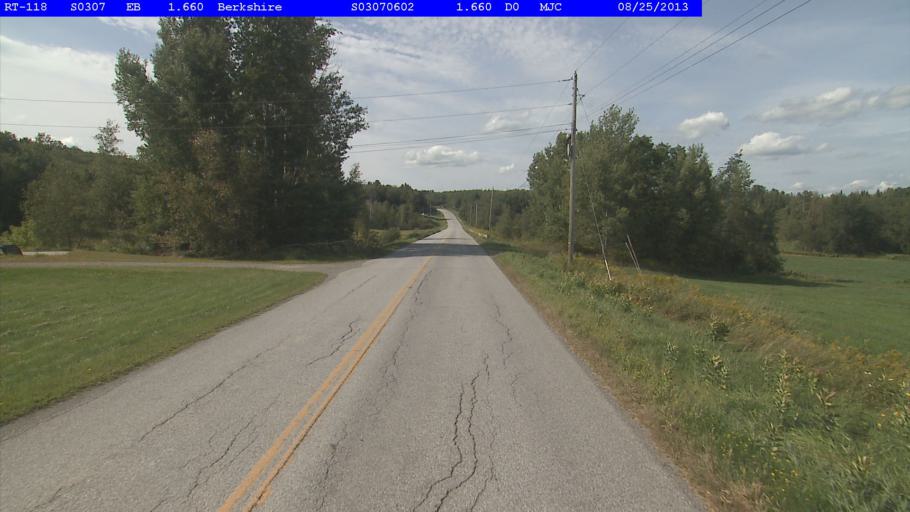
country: US
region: Vermont
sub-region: Franklin County
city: Enosburg Falls
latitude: 44.9437
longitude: -72.7402
